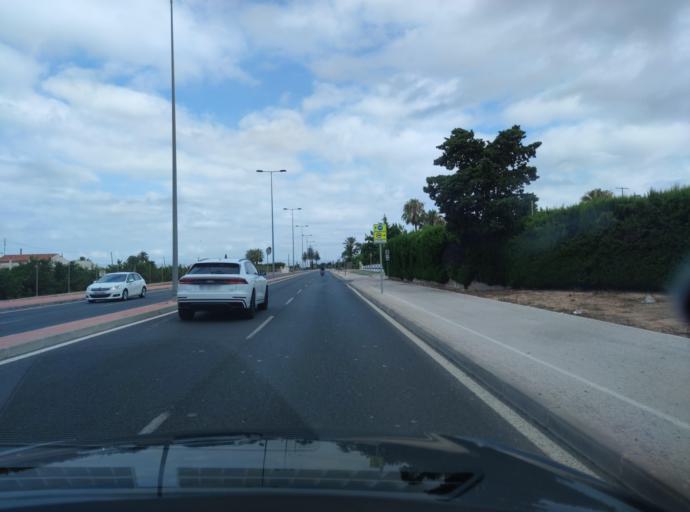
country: ES
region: Valencia
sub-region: Provincia de Alicante
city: Santa Pola
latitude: 38.2034
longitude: -0.5761
